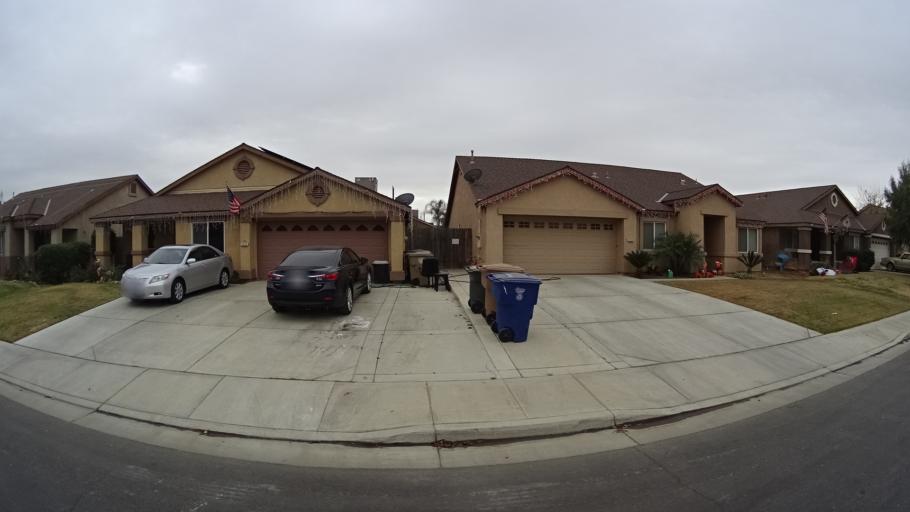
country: US
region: California
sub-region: Kern County
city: Greenfield
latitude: 35.2877
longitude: -119.0313
